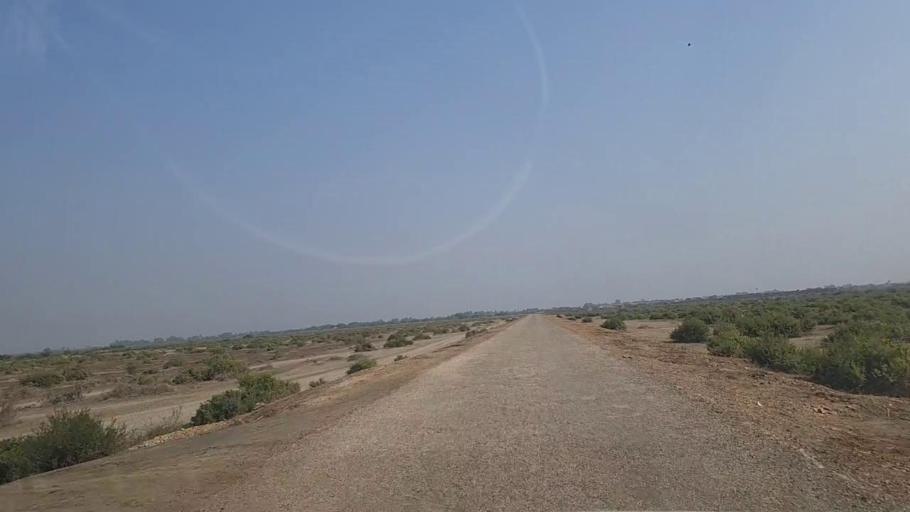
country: PK
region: Sindh
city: Keti Bandar
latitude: 24.2401
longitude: 67.6854
